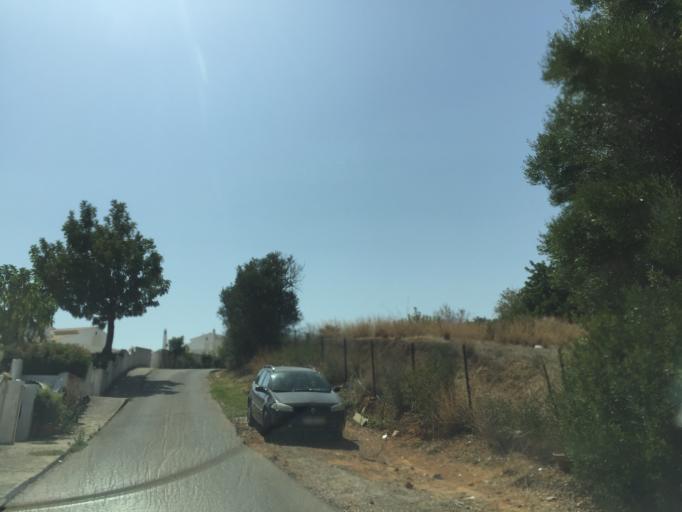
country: PT
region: Faro
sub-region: Albufeira
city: Ferreiras
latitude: 37.1078
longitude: -8.1956
